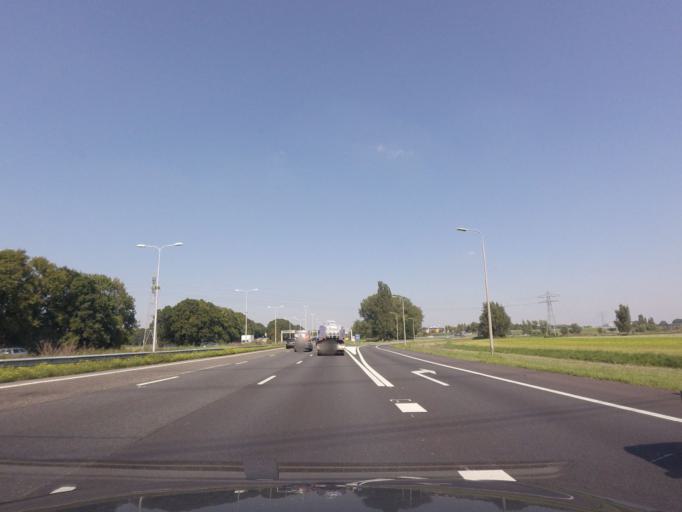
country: NL
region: South Holland
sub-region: Gemeente Dordrecht
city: Dordrecht
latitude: 51.7679
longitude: 4.6482
